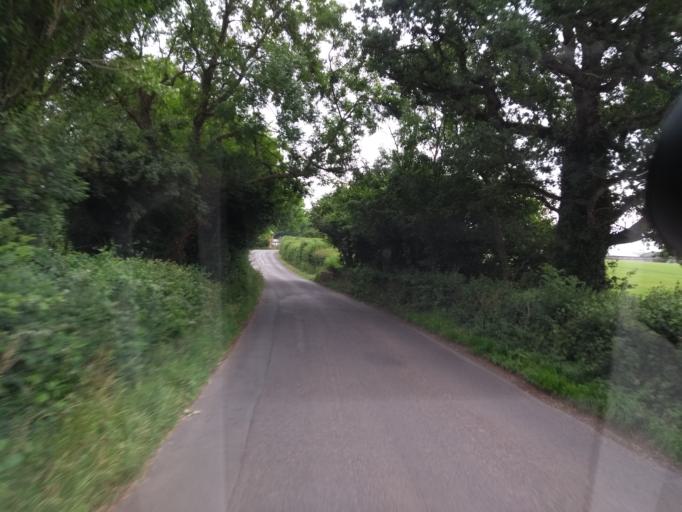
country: GB
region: England
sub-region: Somerset
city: Bishops Lydeard
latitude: 51.0531
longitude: -3.2031
